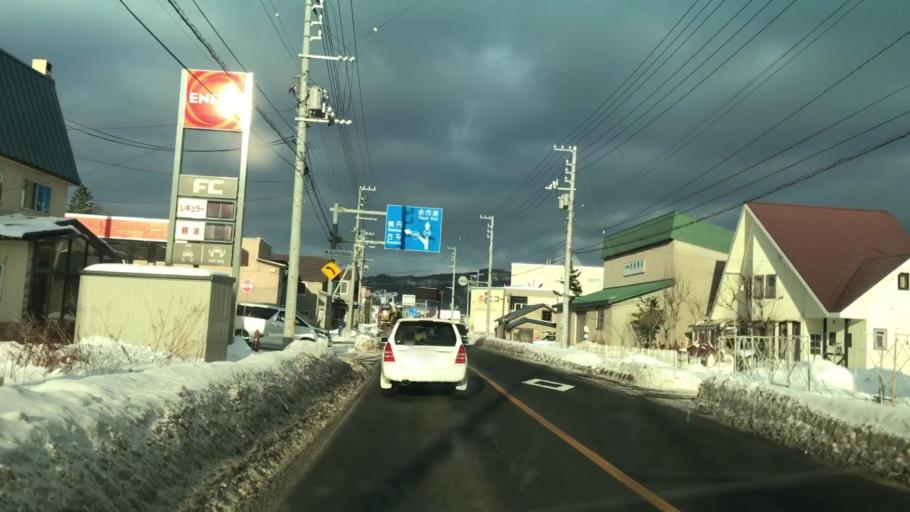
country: JP
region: Hokkaido
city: Yoichi
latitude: 43.2010
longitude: 140.7774
